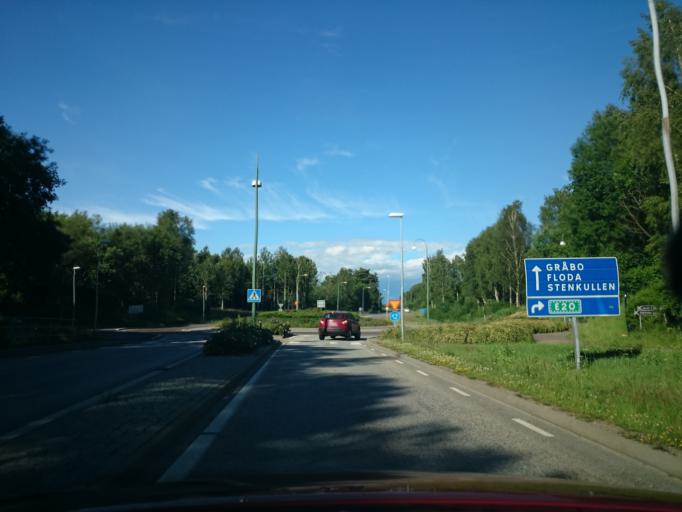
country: SE
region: Vaestra Goetaland
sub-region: Lerums Kommun
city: Lerum
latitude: 57.7773
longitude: 12.2844
